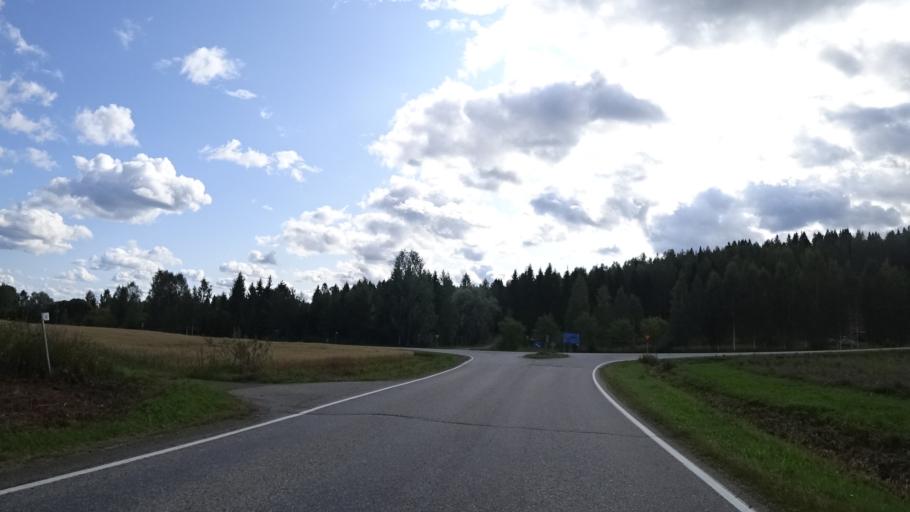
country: RU
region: Republic of Karelia
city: Vyartsilya
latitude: 62.2136
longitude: 30.6002
